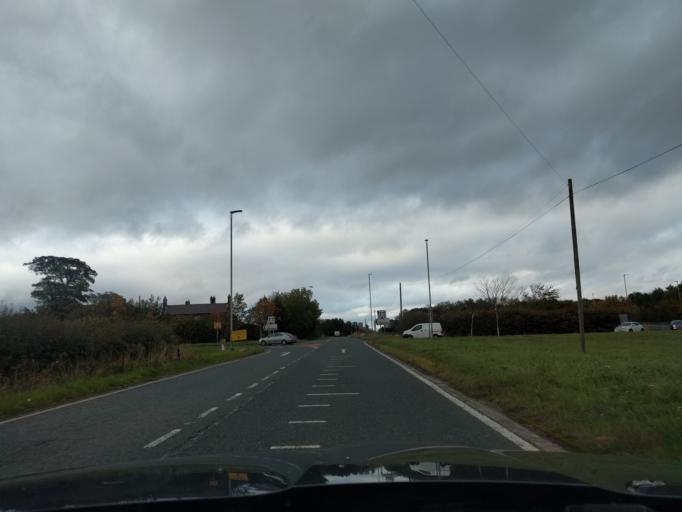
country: GB
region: England
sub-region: Northumberland
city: Cramlington
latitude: 55.0850
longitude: -1.6263
